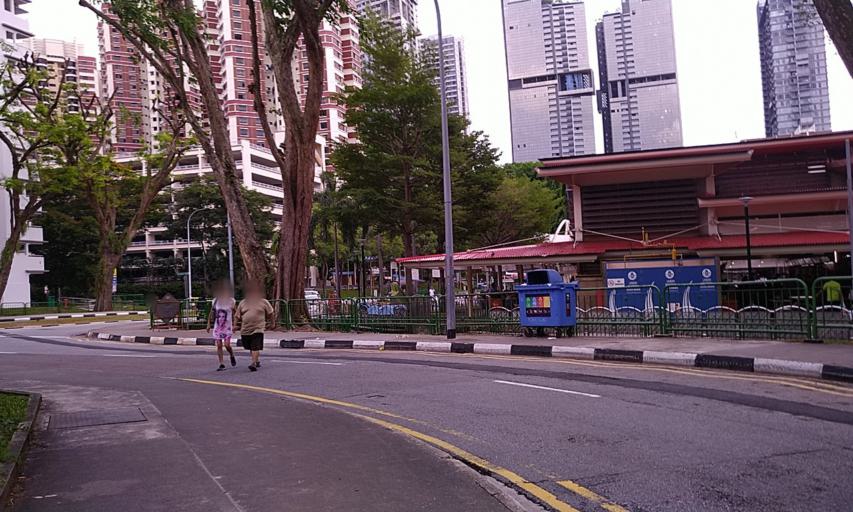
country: SG
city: Singapore
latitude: 1.2869
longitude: 103.8181
